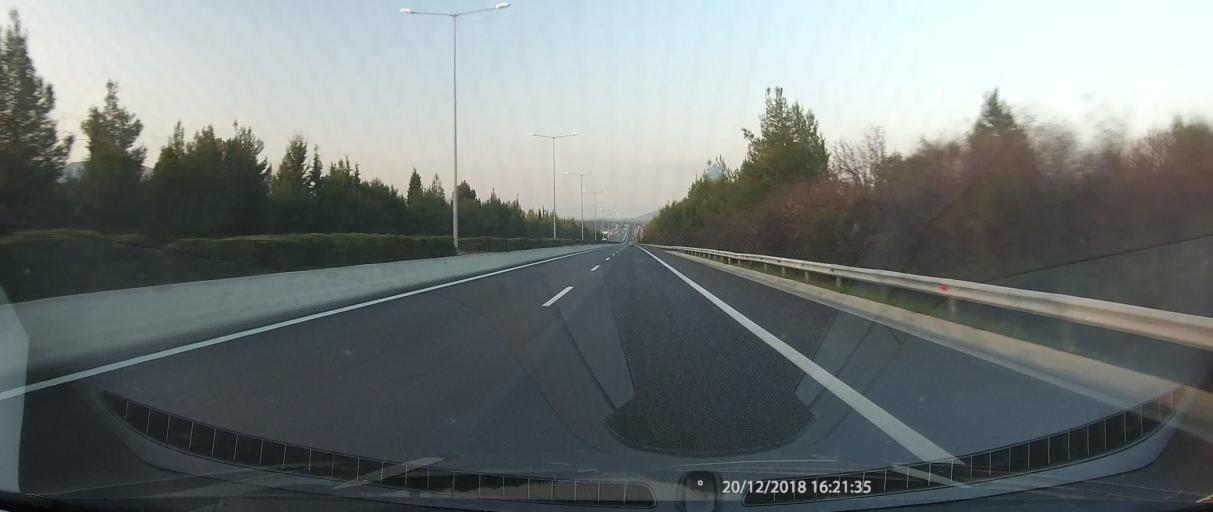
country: GR
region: Thessaly
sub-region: Nomos Magnisias
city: Sourpi
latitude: 39.0513
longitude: 22.8918
